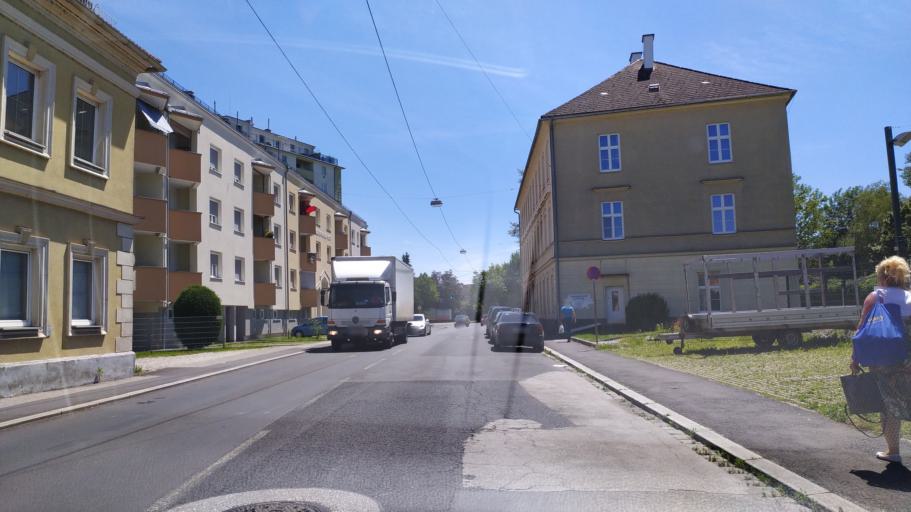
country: AT
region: Upper Austria
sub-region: Politischer Bezirk Linz-Land
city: Ansfelden
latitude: 48.2527
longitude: 14.3141
